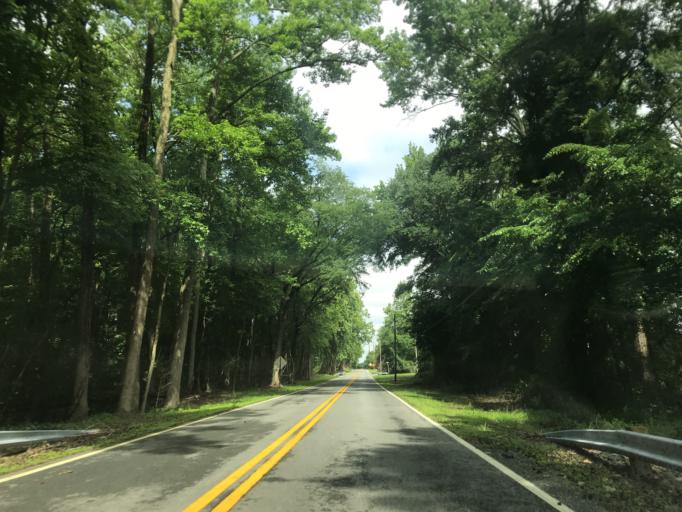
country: US
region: Maryland
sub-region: Caroline County
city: Ridgely
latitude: 38.8860
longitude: -75.9810
